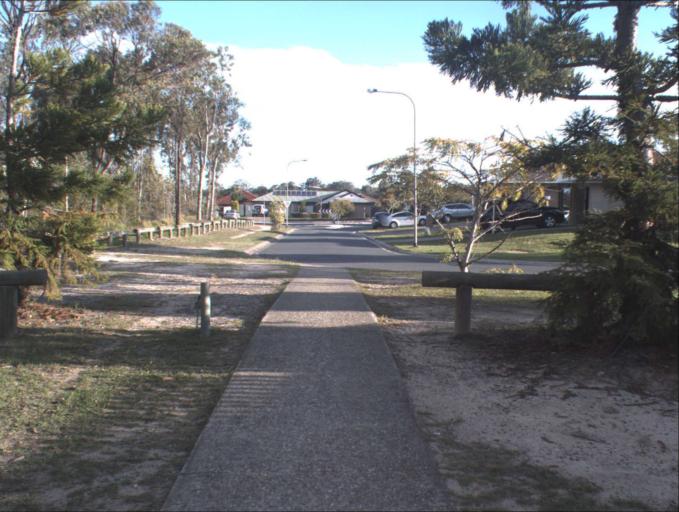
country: AU
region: Queensland
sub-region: Logan
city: Logan Reserve
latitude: -27.6934
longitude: 153.0868
